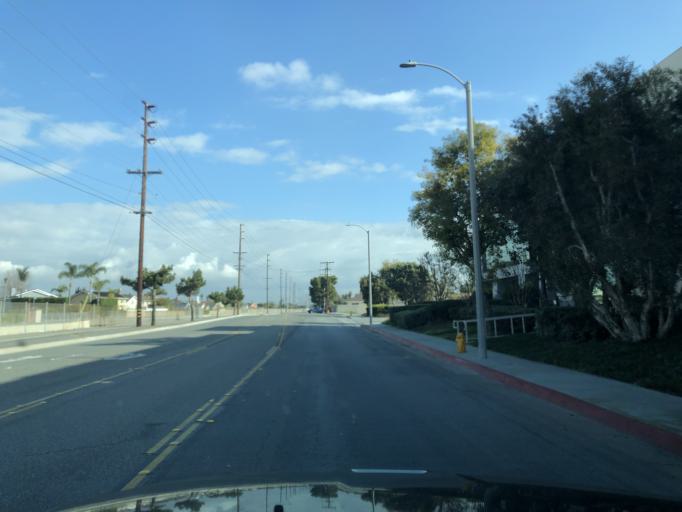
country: US
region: California
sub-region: Orange County
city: Westminster
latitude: 33.7539
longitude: -118.0366
